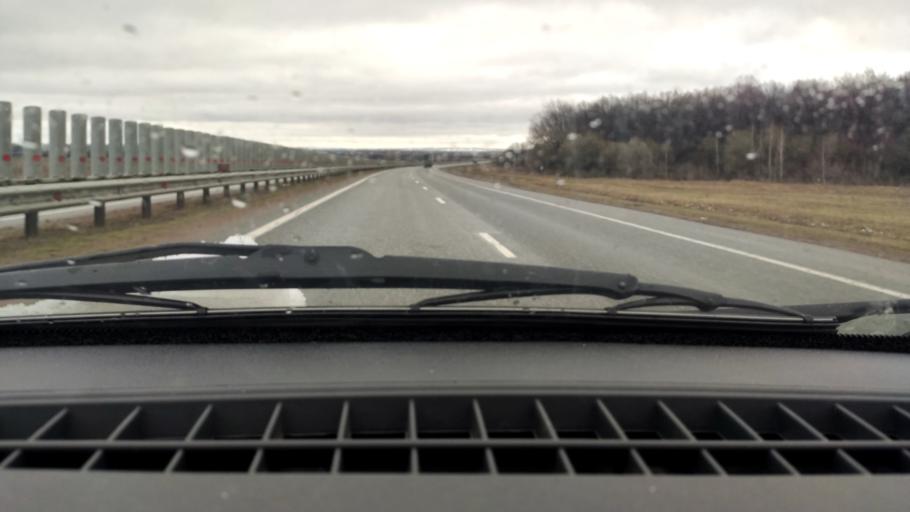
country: RU
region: Bashkortostan
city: Kushnarenkovo
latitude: 55.0667
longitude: 55.3376
